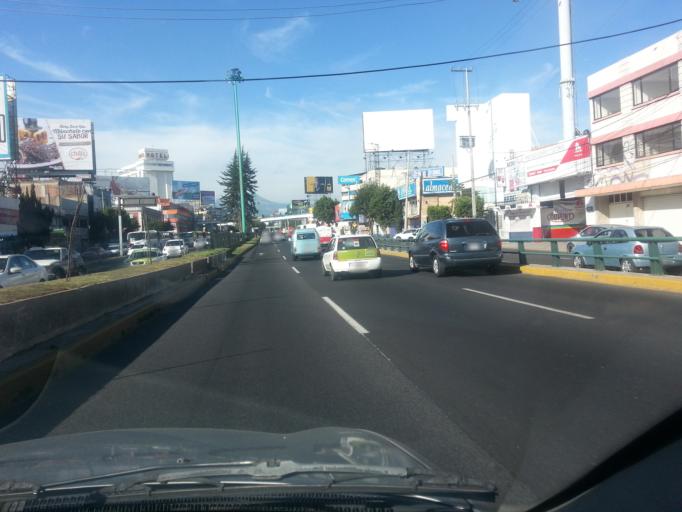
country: MX
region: Mexico
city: Toluca
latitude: 19.2807
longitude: -99.6425
